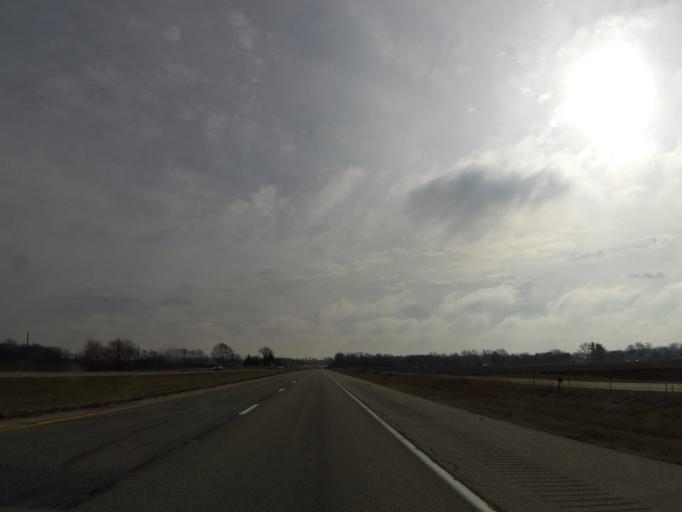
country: US
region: Indiana
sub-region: Hancock County
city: New Palestine
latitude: 39.6170
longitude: -85.8681
